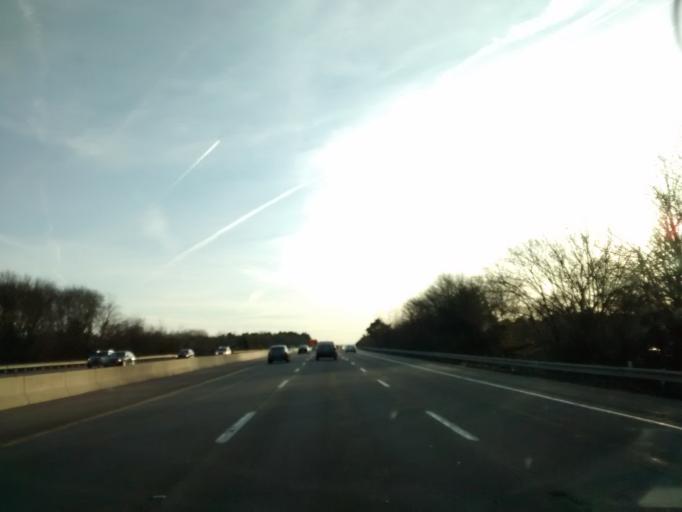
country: US
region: Massachusetts
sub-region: Worcester County
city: Cordaville
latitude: 42.2817
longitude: -71.5115
